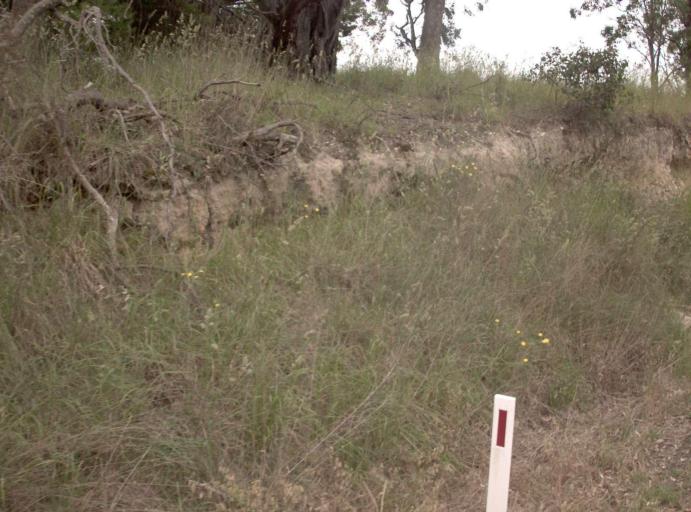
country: AU
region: Victoria
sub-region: East Gippsland
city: Bairnsdale
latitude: -37.7775
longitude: 147.3237
